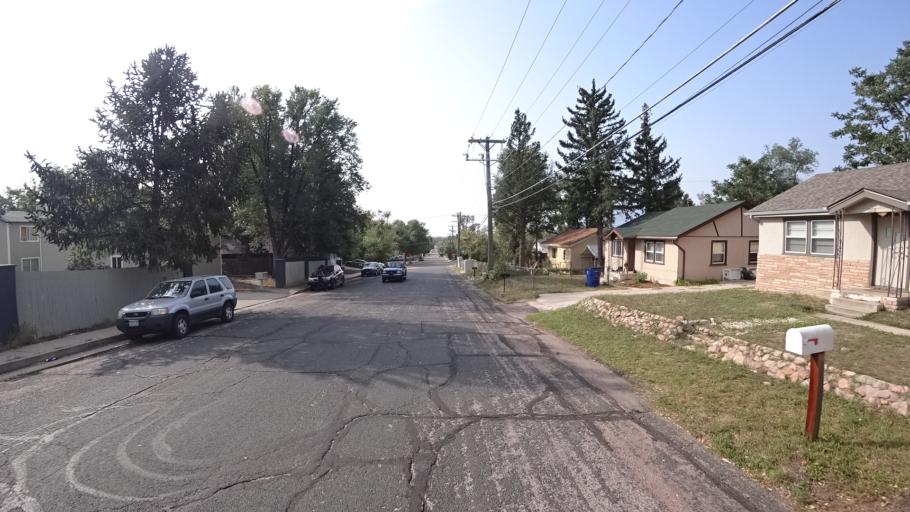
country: US
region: Colorado
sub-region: El Paso County
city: Colorado Springs
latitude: 38.8478
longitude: -104.7804
